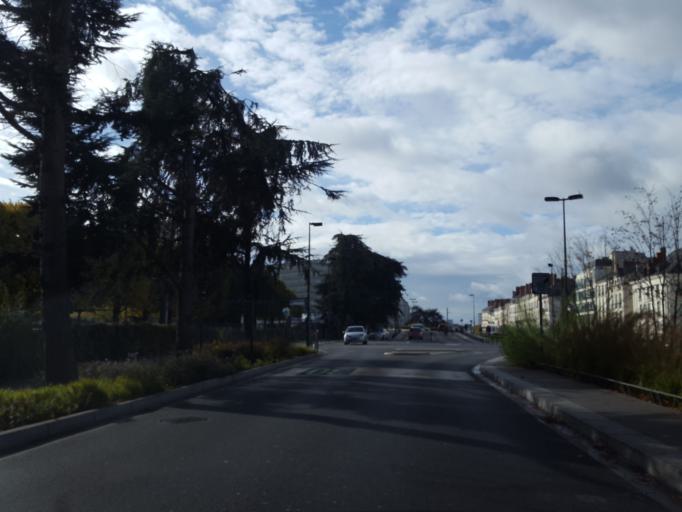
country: FR
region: Pays de la Loire
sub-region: Departement de la Loire-Atlantique
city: Nantes
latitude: 47.2135
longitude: -1.5519
